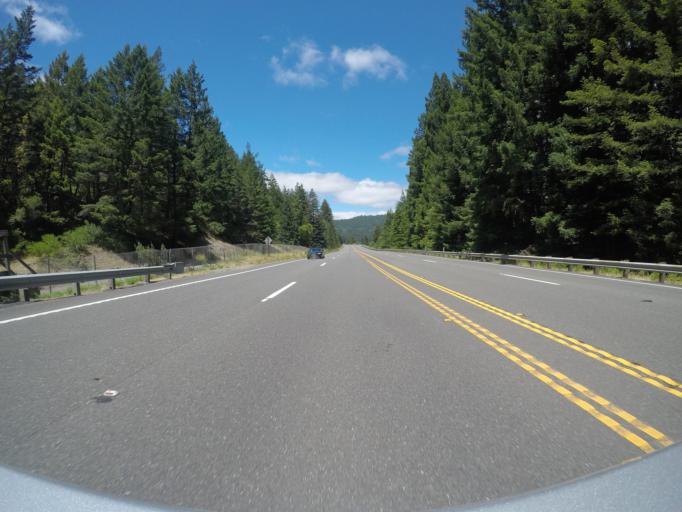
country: US
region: California
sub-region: Humboldt County
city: Redway
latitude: 40.2363
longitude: -123.8332
